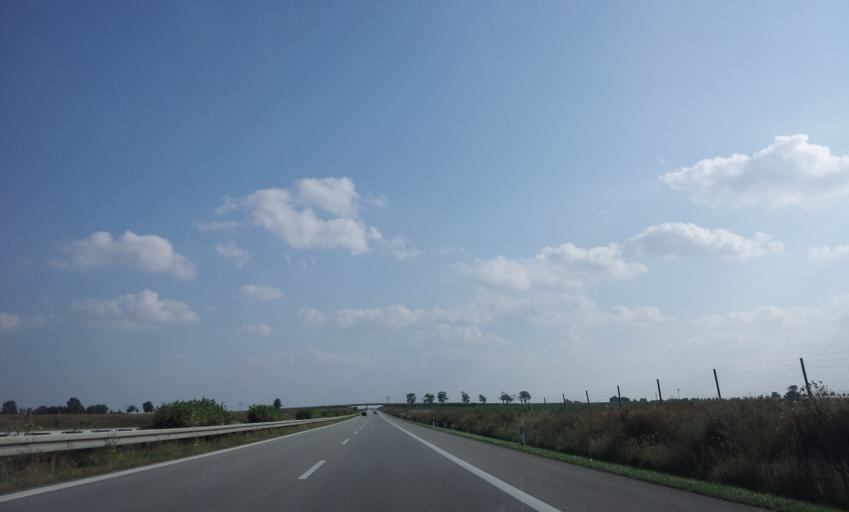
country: DE
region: Mecklenburg-Vorpommern
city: Burow
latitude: 53.8315
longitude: 13.3263
